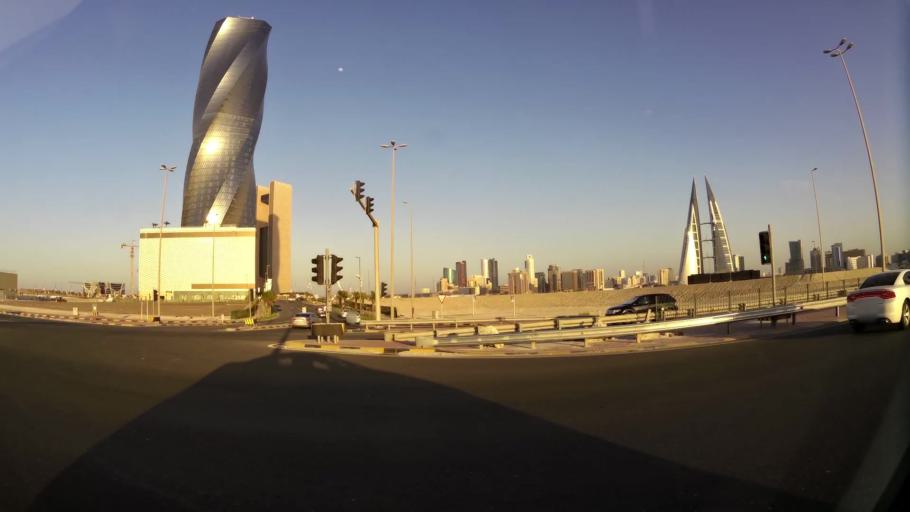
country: BH
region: Manama
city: Manama
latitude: 26.2456
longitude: 50.5743
